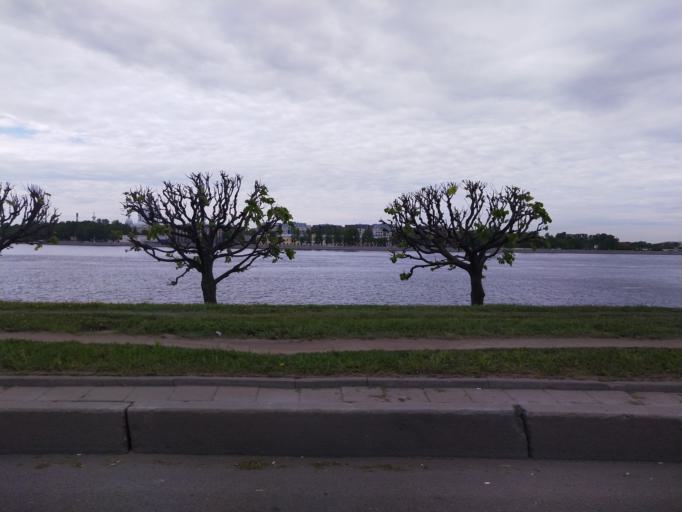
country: RU
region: Leningrad
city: Finlyandskiy
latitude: 59.9569
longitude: 30.4043
